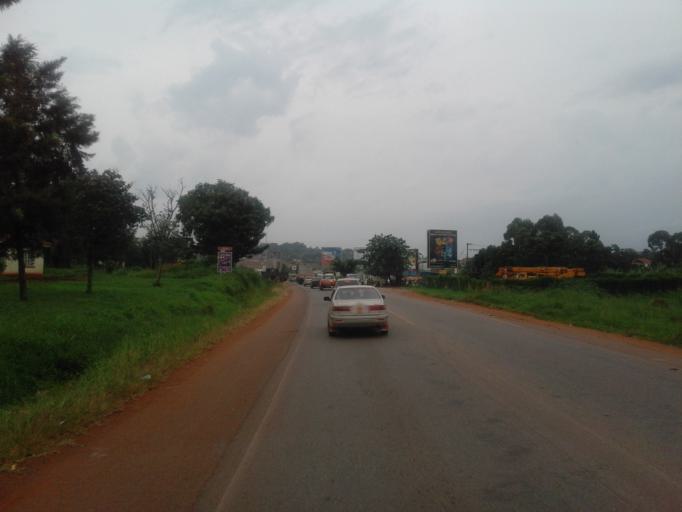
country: UG
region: Eastern Region
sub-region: Jinja District
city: Jinja
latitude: 0.4445
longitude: 33.1959
